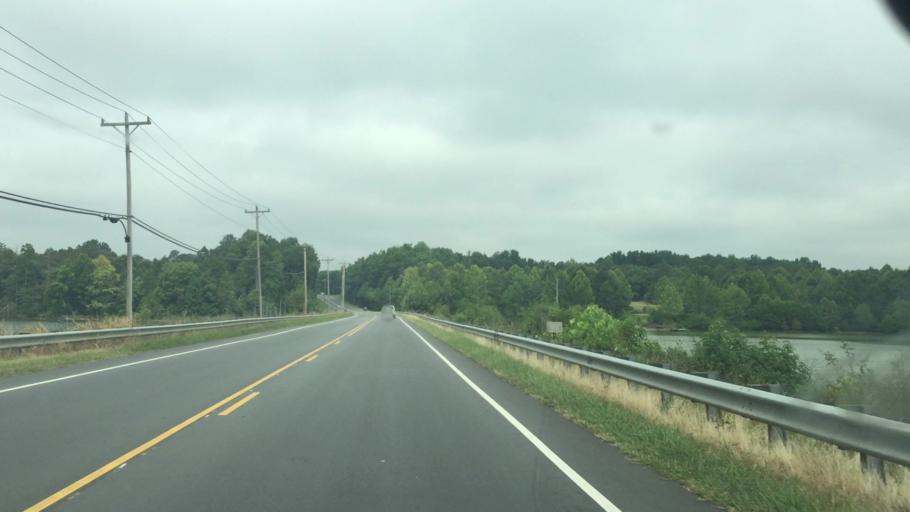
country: US
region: North Carolina
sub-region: Rowan County
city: Enochville
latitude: 35.4378
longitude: -80.7107
